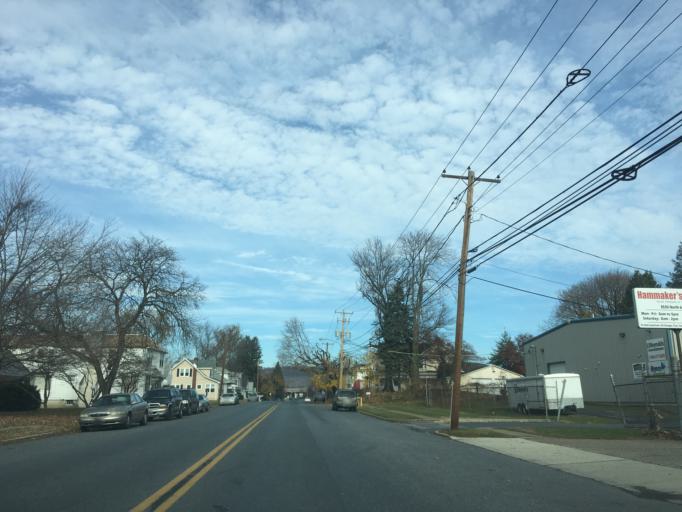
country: US
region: Pennsylvania
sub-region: Dauphin County
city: Harrisburg
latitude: 40.3044
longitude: -76.8954
